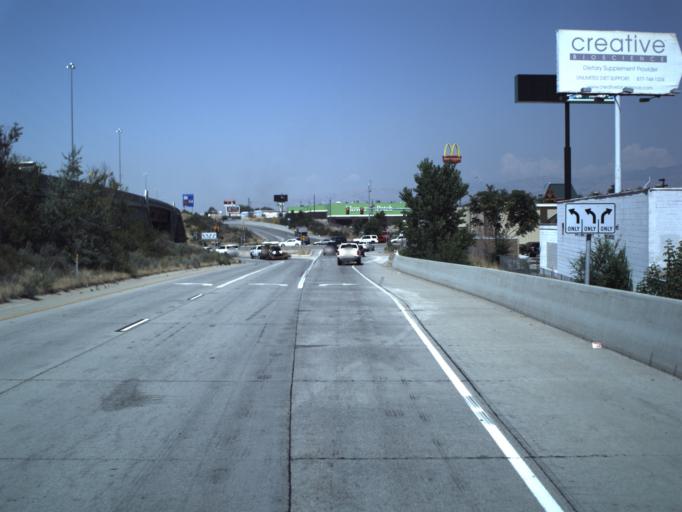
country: US
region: Utah
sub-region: Salt Lake County
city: Murray
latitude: 40.6728
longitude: -111.9009
